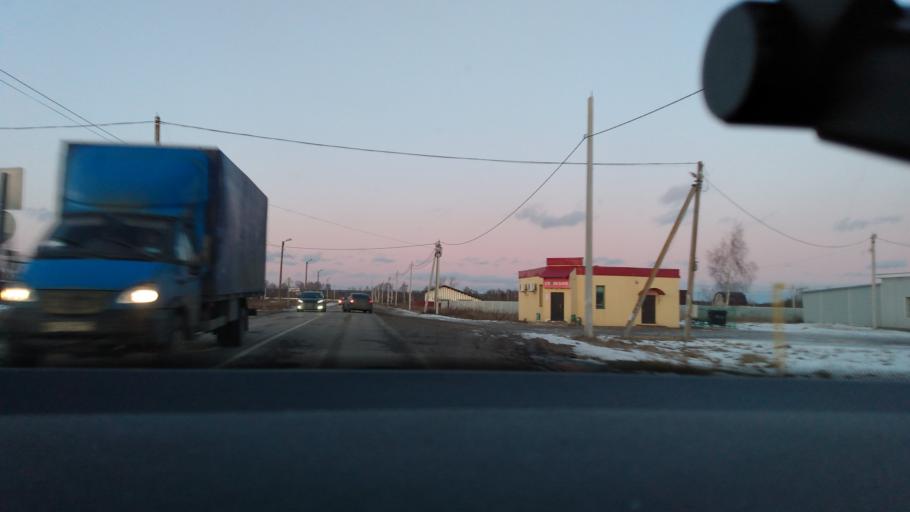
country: RU
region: Moskovskaya
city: Krasnaya Poyma
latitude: 55.1215
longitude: 39.0749
